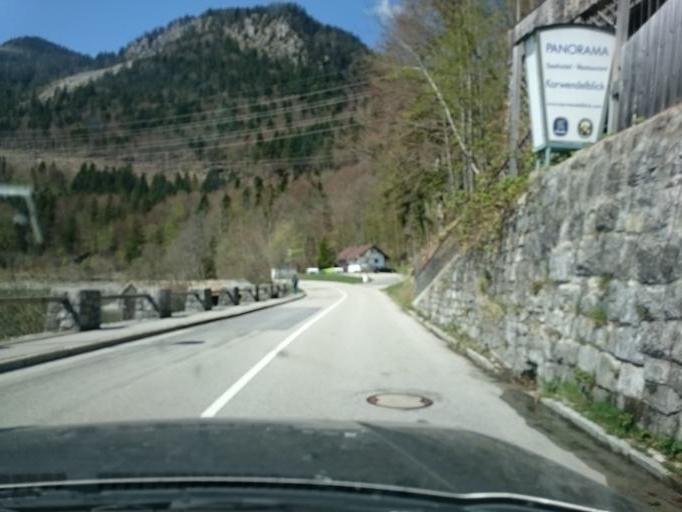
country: DE
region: Bavaria
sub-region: Upper Bavaria
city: Schlehdorf
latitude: 47.6145
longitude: 11.3416
